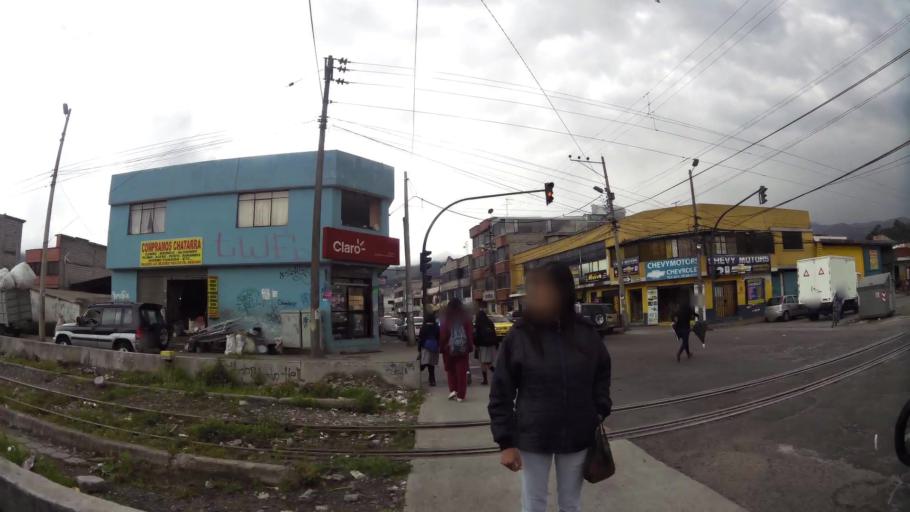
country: EC
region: Pichincha
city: Quito
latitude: -0.2762
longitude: -78.5334
